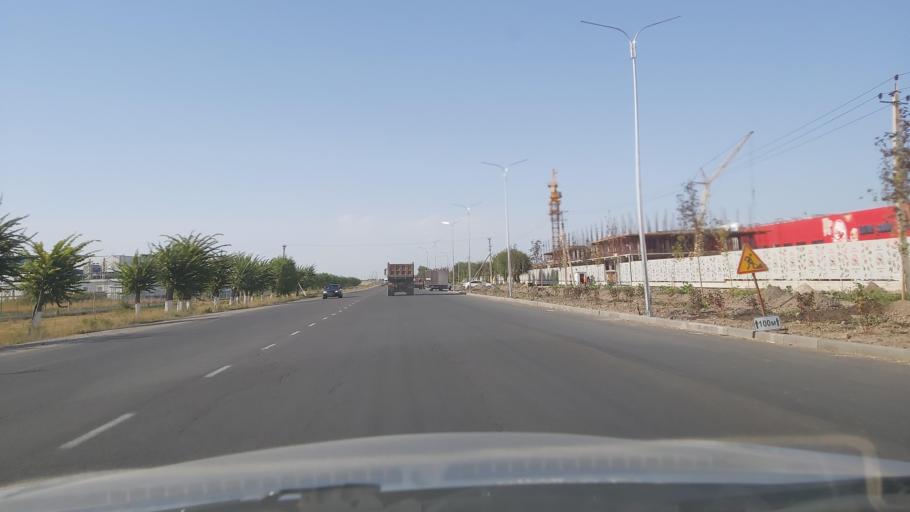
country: KZ
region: Almaty Oblysy
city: Energeticheskiy
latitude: 43.4587
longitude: 77.0337
